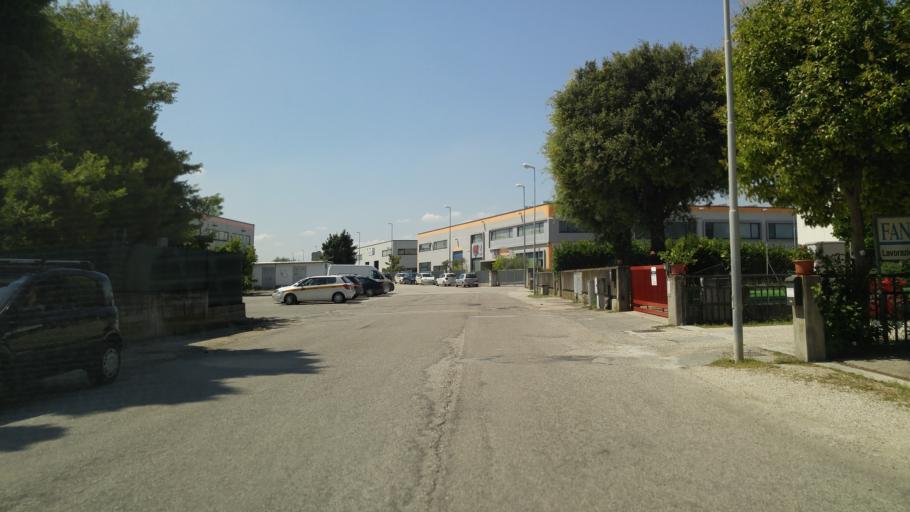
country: IT
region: The Marches
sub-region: Provincia di Pesaro e Urbino
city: Fano
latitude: 43.8256
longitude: 13.0373
